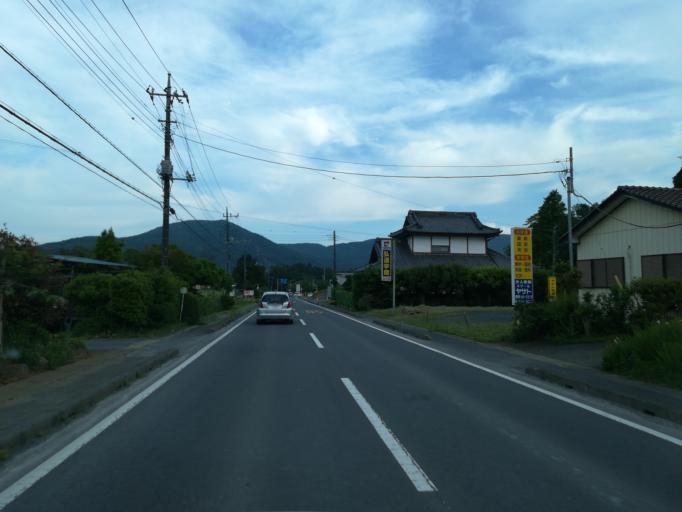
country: JP
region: Ibaraki
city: Tsukuba
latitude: 36.2082
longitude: 140.1782
